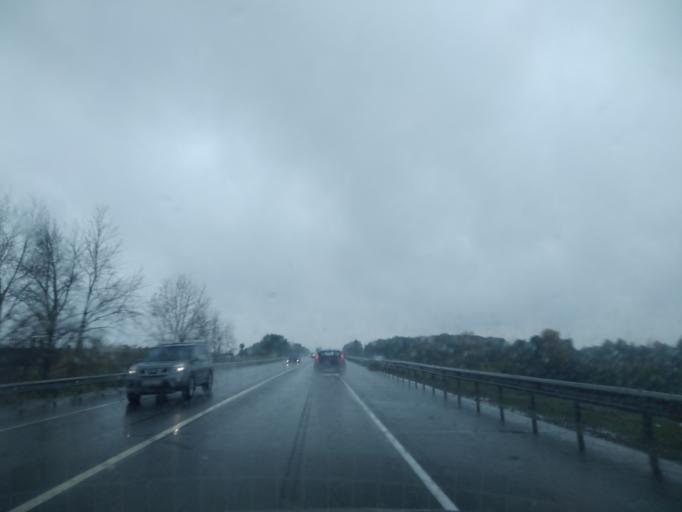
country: RU
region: Tula
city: Pervomayskiy
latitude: 54.0183
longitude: 37.4840
